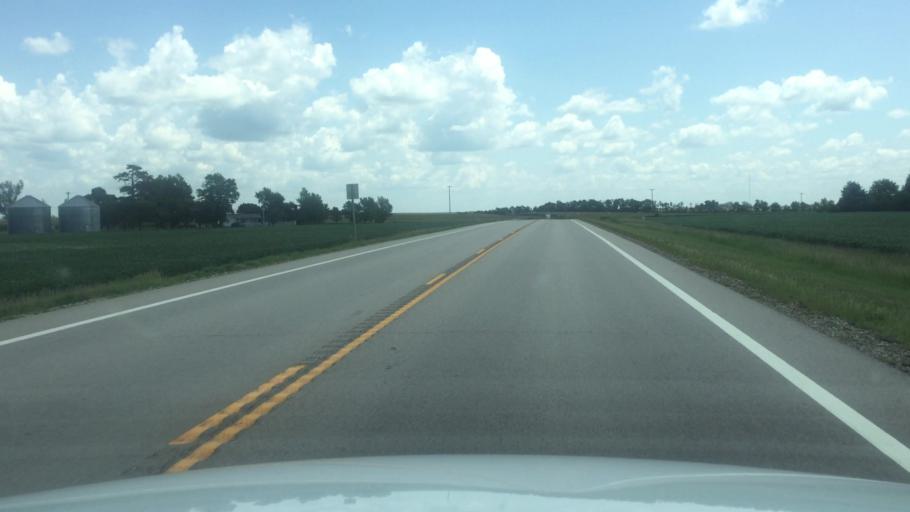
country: US
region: Kansas
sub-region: Brown County
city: Horton
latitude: 39.6654
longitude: -95.4178
